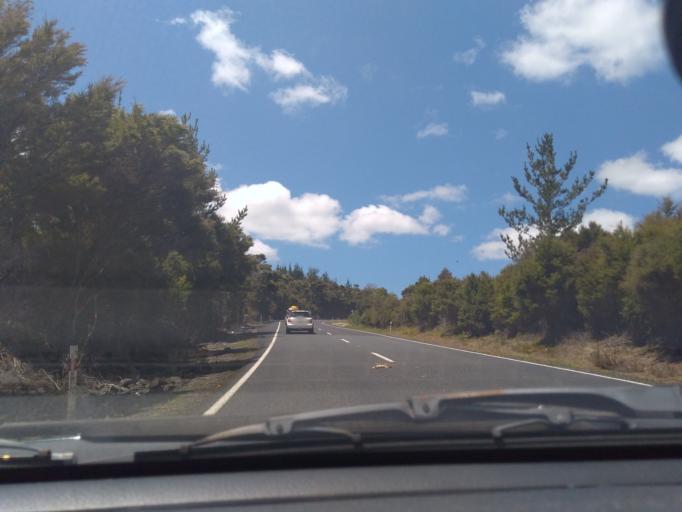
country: NZ
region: Northland
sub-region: Far North District
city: Kerikeri
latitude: -35.1214
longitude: 173.8485
